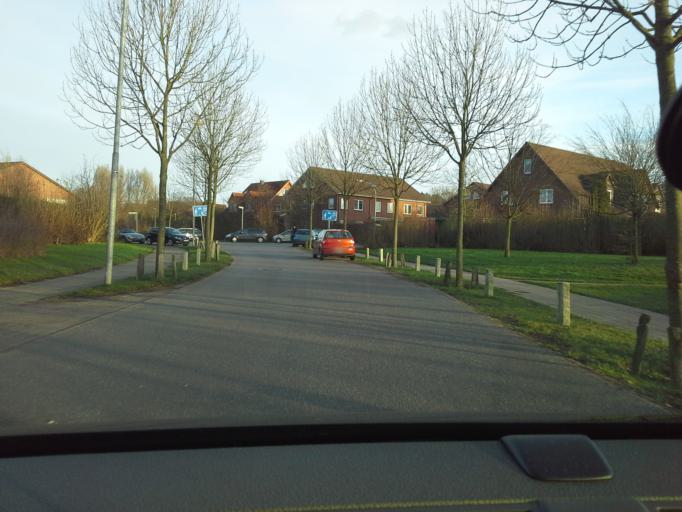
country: DE
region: Schleswig-Holstein
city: Quickborn
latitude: 53.7253
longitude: 9.8912
